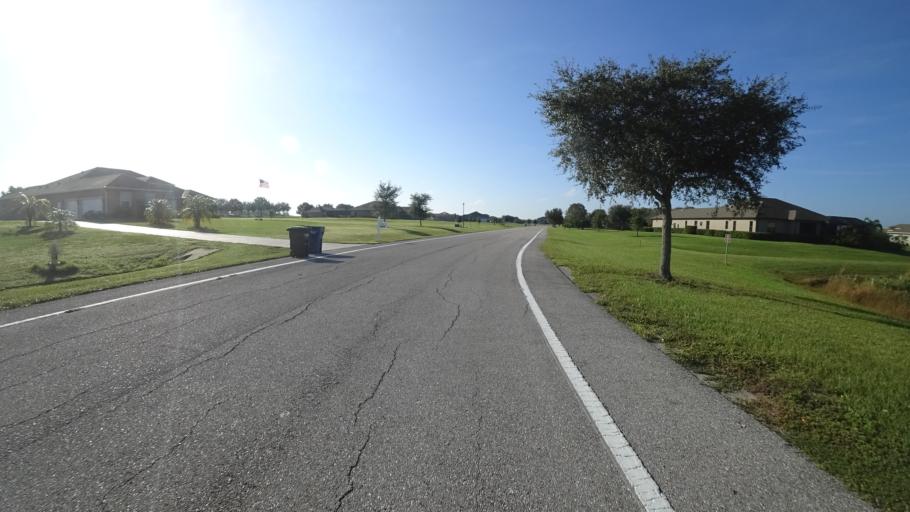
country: US
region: Florida
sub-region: Hillsborough County
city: Sun City Center
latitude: 27.5759
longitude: -82.3534
